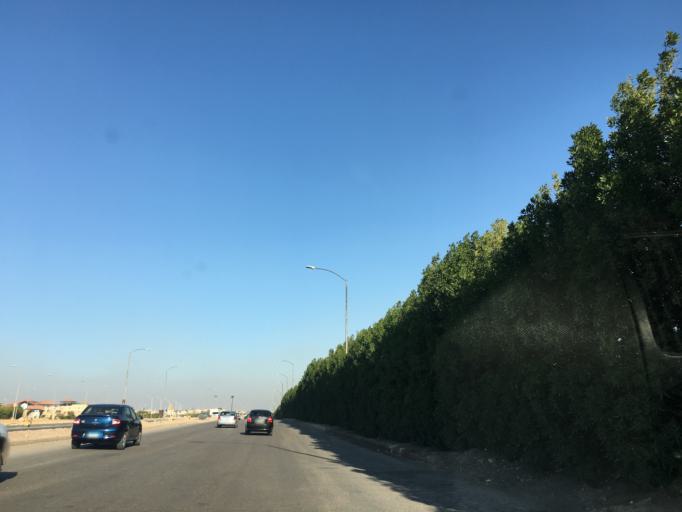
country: EG
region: Al Jizah
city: Madinat Sittah Uktubar
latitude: 29.9936
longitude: 30.9494
